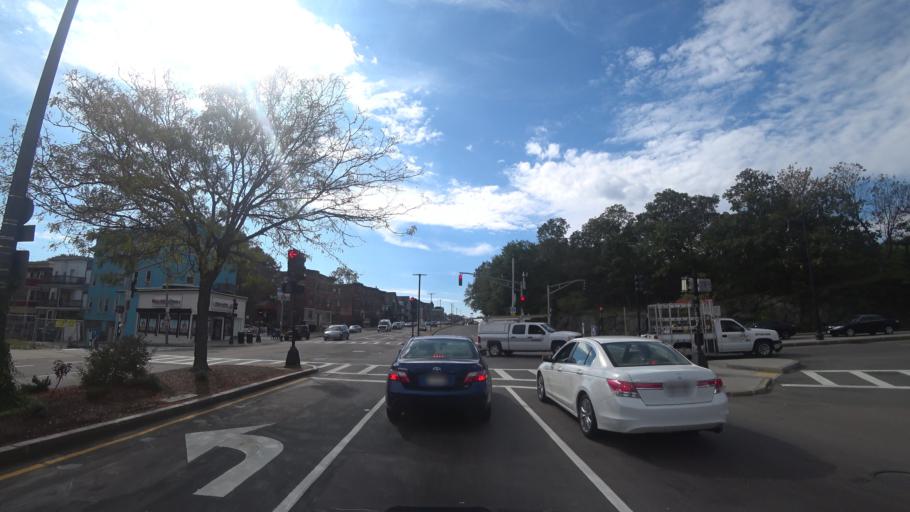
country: US
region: Massachusetts
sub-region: Suffolk County
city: Jamaica Plain
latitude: 42.3056
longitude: -71.0847
